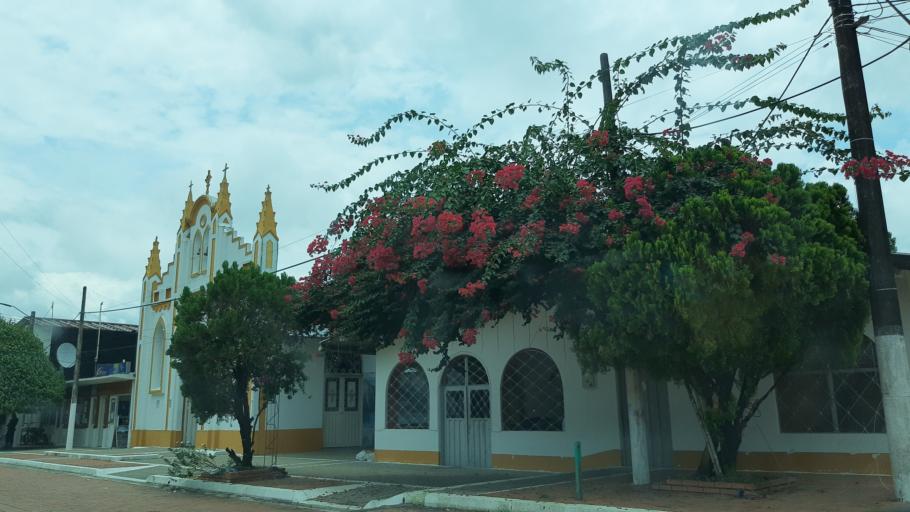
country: CO
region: Casanare
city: Sabanalarga
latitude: 4.8546
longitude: -73.0404
